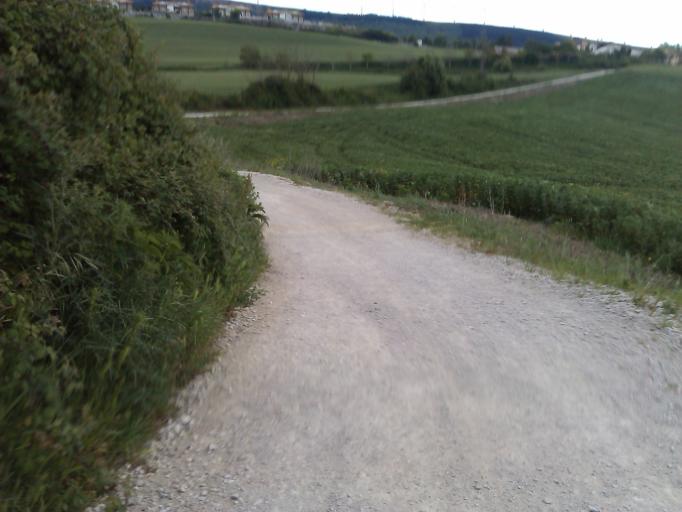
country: ES
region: Navarre
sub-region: Provincia de Navarra
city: Galar
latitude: 42.7505
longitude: -1.7199
